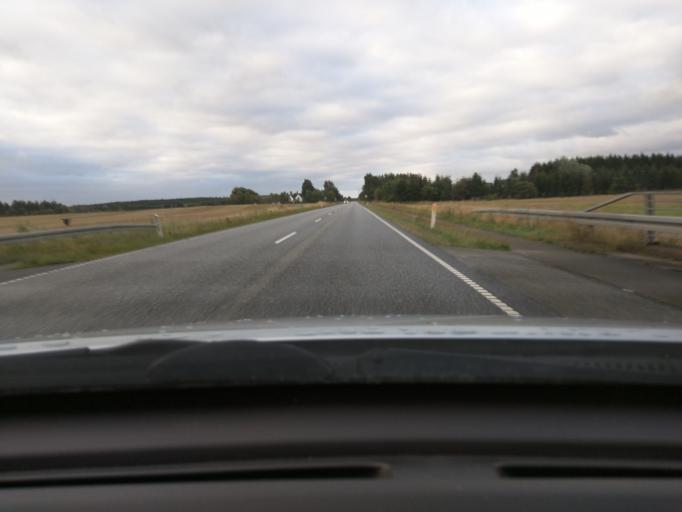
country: DK
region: Central Jutland
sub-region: Ikast-Brande Kommune
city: Bording Kirkeby
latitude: 56.2489
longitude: 9.3211
